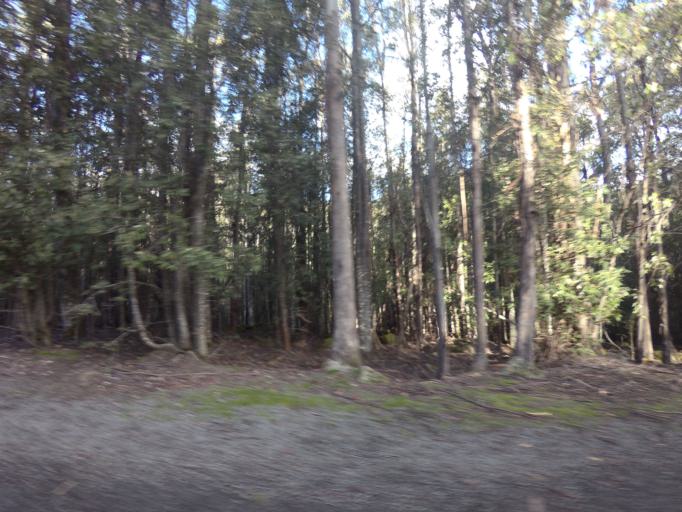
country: AU
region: Tasmania
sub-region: Glenorchy
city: Berriedale
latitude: -42.8574
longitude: 147.1639
